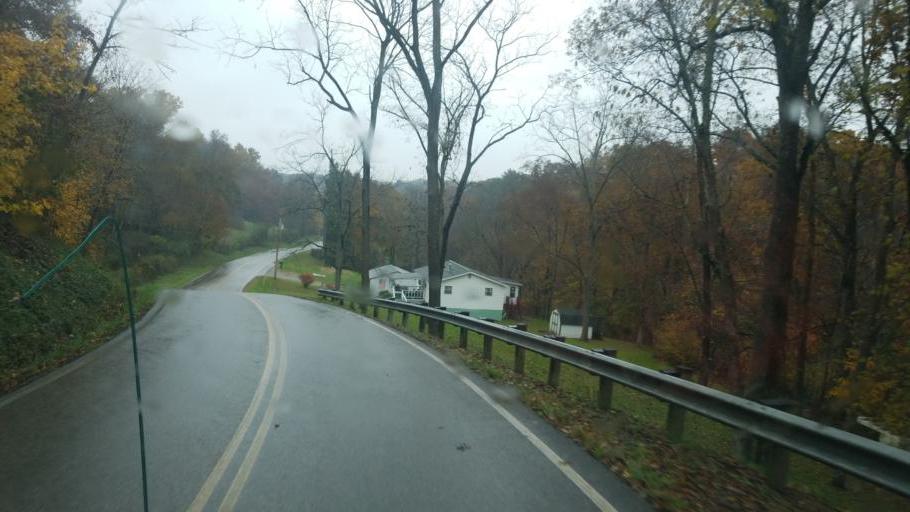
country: US
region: West Virginia
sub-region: Wood County
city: Blennerhassett
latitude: 39.3239
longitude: -81.6221
